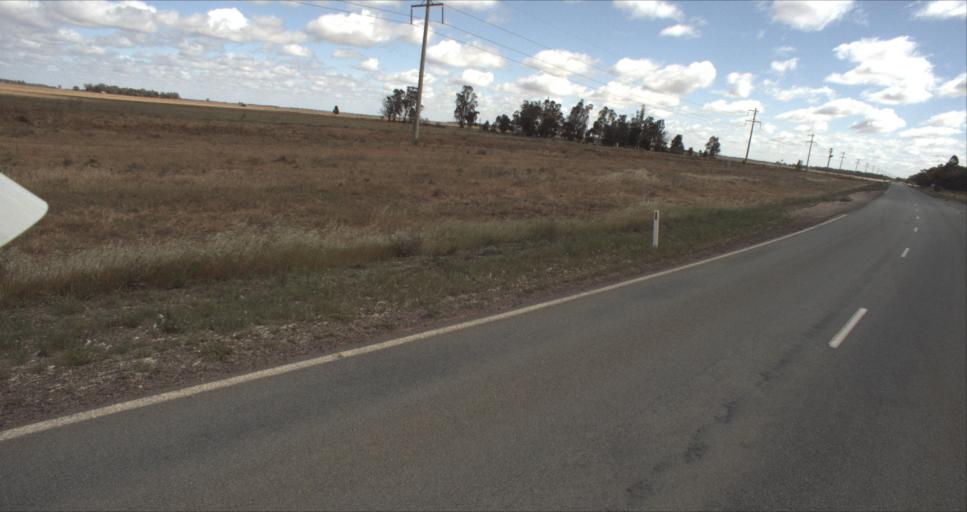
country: AU
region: New South Wales
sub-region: Murrumbidgee Shire
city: Darlington Point
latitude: -34.5951
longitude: 146.1629
